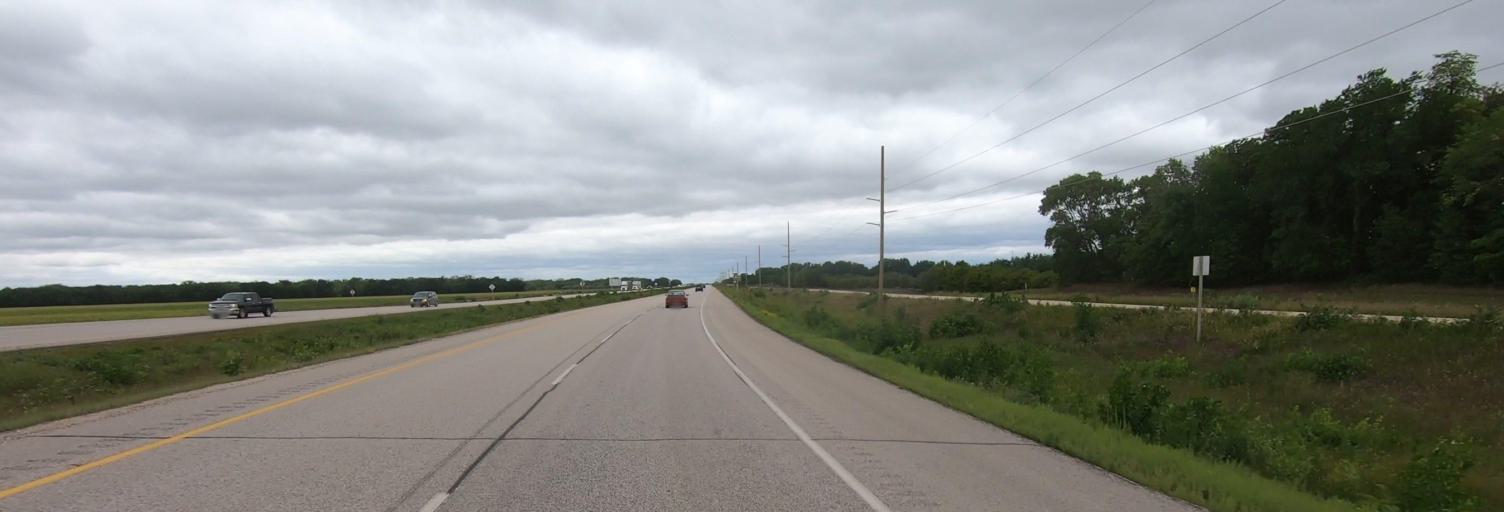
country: CA
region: Manitoba
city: Portage la Prairie
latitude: 49.9466
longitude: -98.3012
